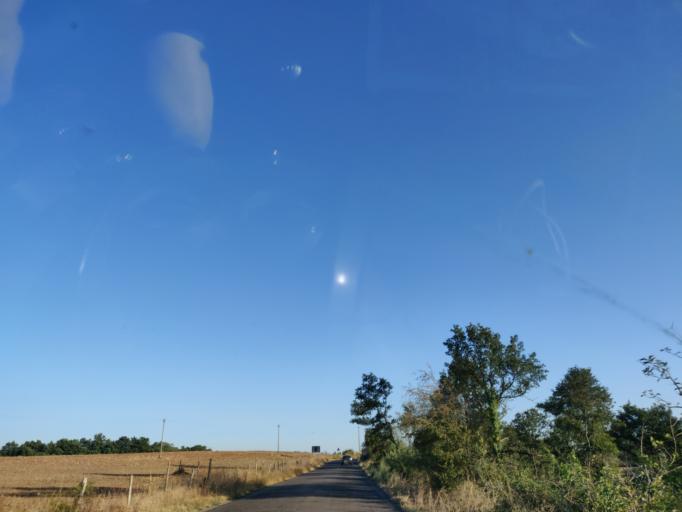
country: IT
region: Latium
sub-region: Provincia di Viterbo
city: Acquapendente
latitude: 42.7102
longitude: 11.8787
